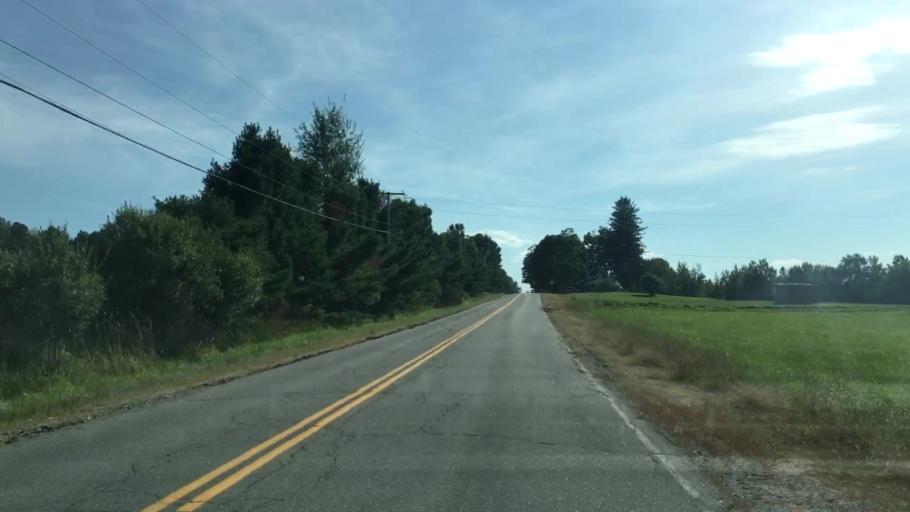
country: US
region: Maine
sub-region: Penobscot County
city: Lincoln
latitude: 45.3207
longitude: -68.5339
